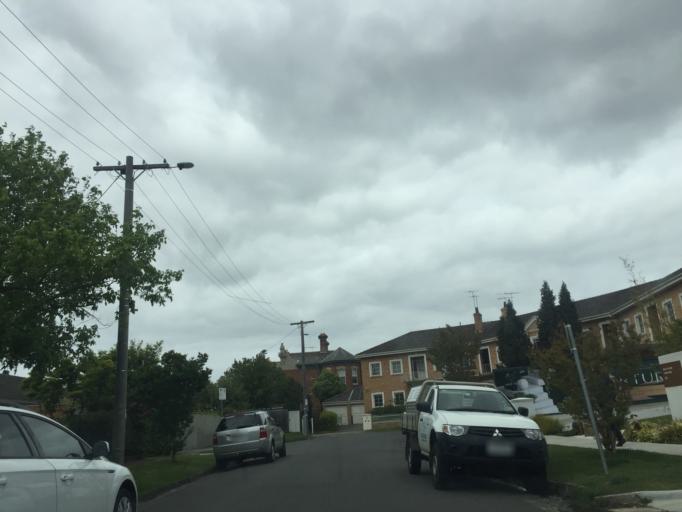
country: AU
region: Victoria
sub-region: Boroondara
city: Kew
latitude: -37.8082
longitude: 145.0398
